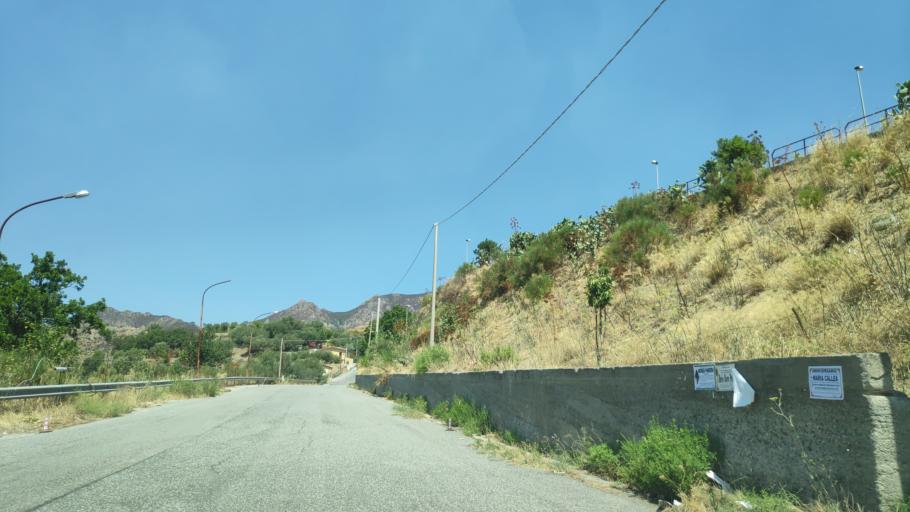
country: IT
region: Calabria
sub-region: Provincia di Reggio Calabria
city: Bova
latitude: 37.9860
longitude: 15.9292
